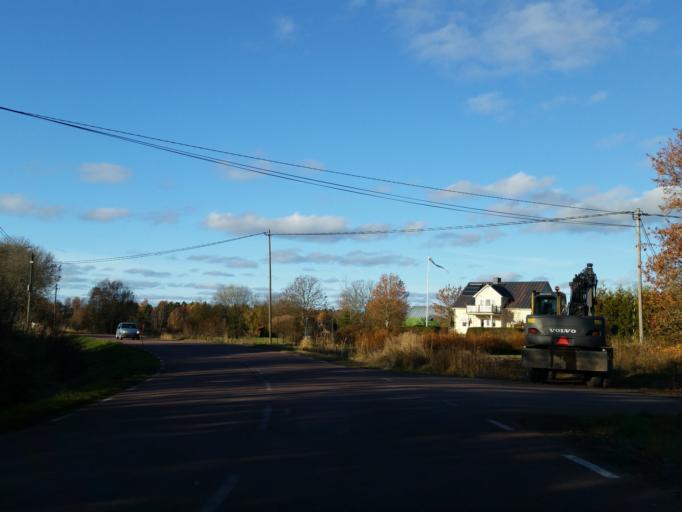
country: AX
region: Alands landsbygd
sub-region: Finstroem
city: Finstroem
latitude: 60.3332
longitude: 19.9494
